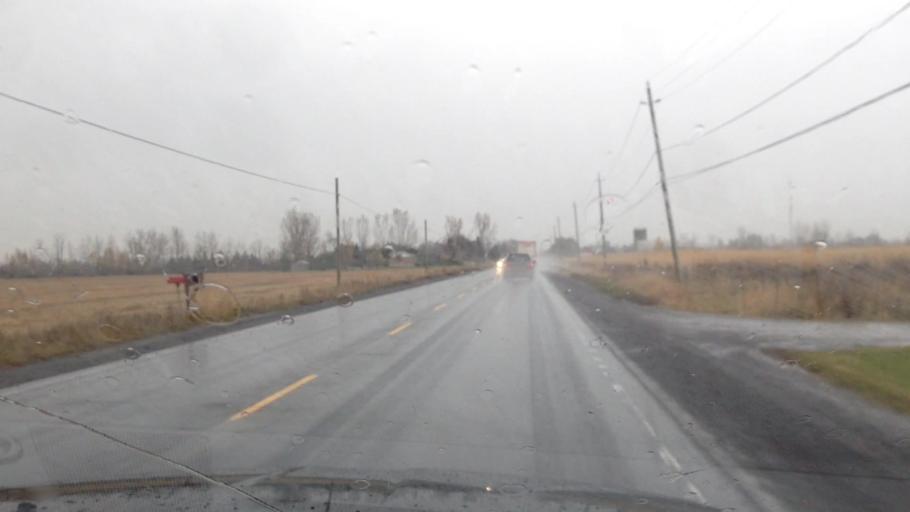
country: CA
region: Ontario
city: Bourget
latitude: 45.2878
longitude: -75.3211
